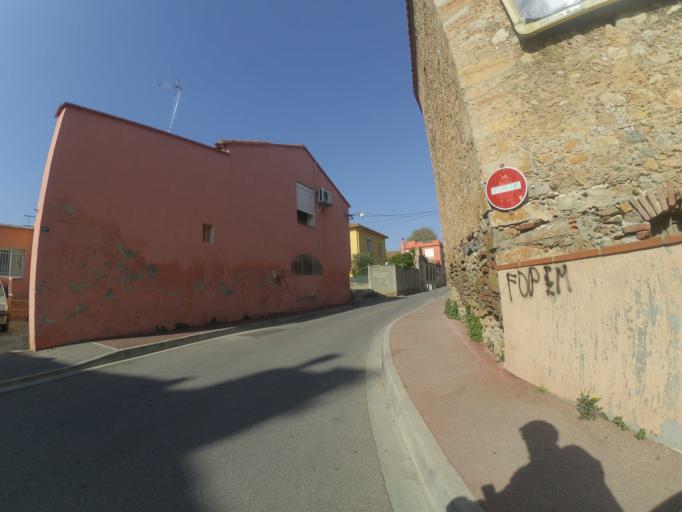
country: FR
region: Languedoc-Roussillon
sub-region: Departement des Pyrenees-Orientales
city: Thuir
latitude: 42.6317
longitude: 2.7555
